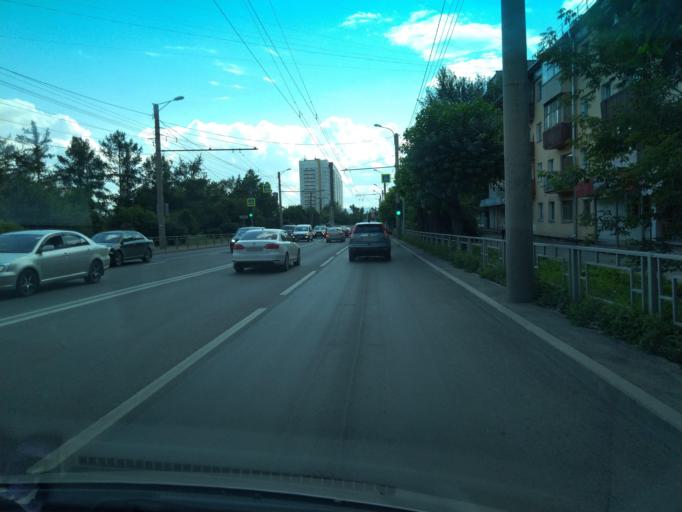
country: RU
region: Krasnoyarskiy
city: Solnechnyy
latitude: 56.0446
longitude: 92.9412
